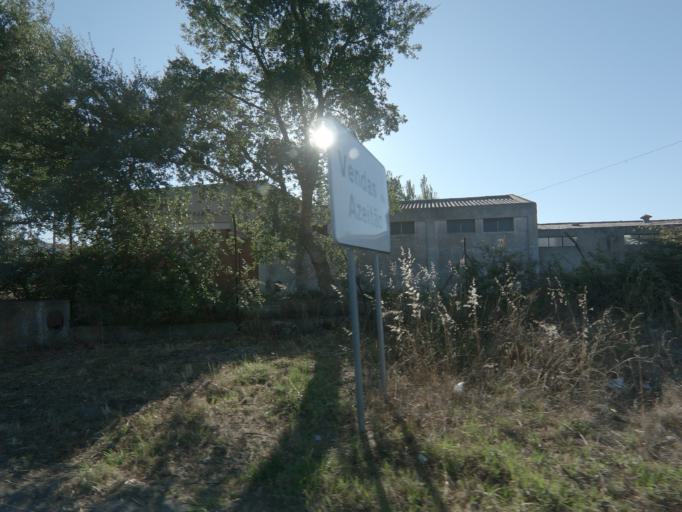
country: PT
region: Setubal
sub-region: Palmela
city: Quinta do Anjo
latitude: 38.5348
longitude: -8.9882
